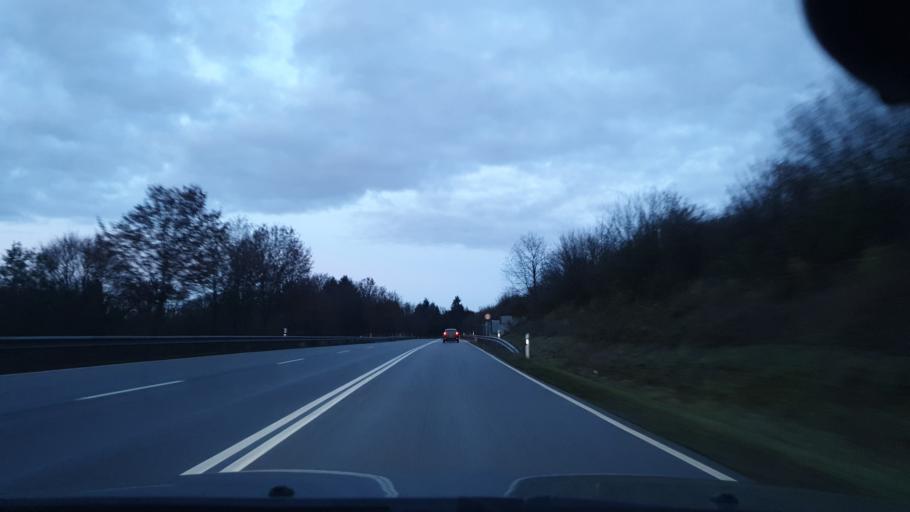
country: DE
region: Rheinland-Pfalz
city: Schopp
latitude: 49.3502
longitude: 7.6821
